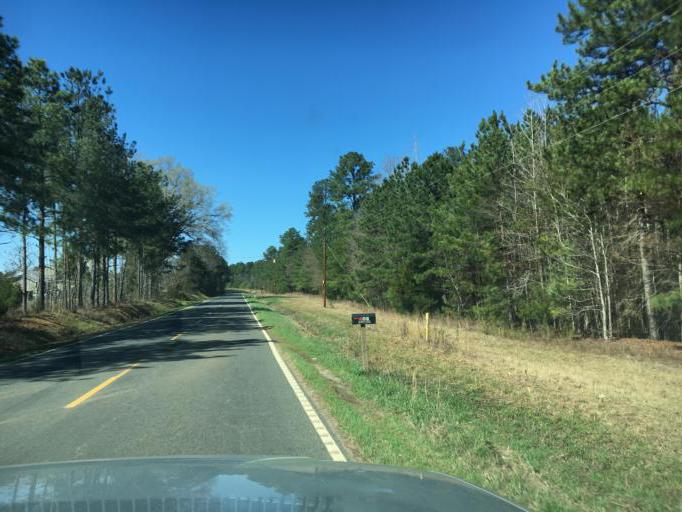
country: US
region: South Carolina
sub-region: Greenwood County
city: Ninety Six
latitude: 34.2861
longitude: -81.9564
